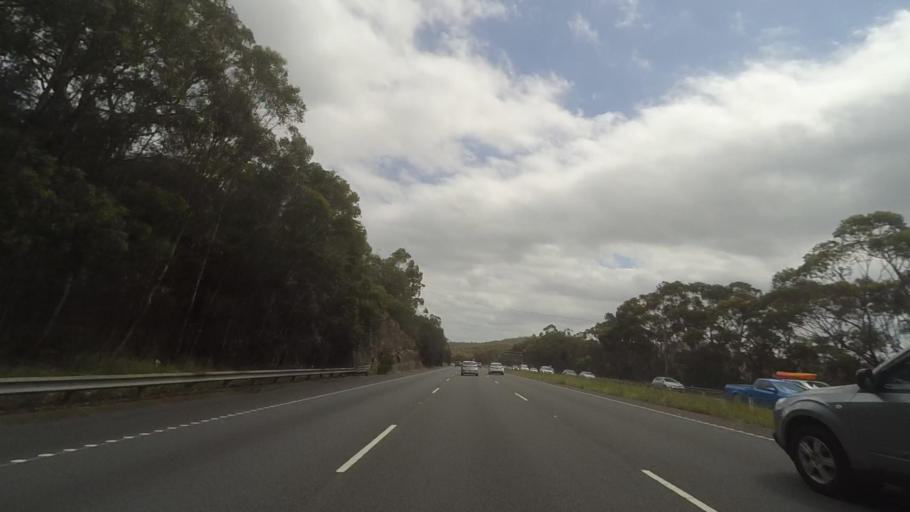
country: AU
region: New South Wales
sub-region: Gosford Shire
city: Point Clare
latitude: -33.4361
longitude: 151.2208
